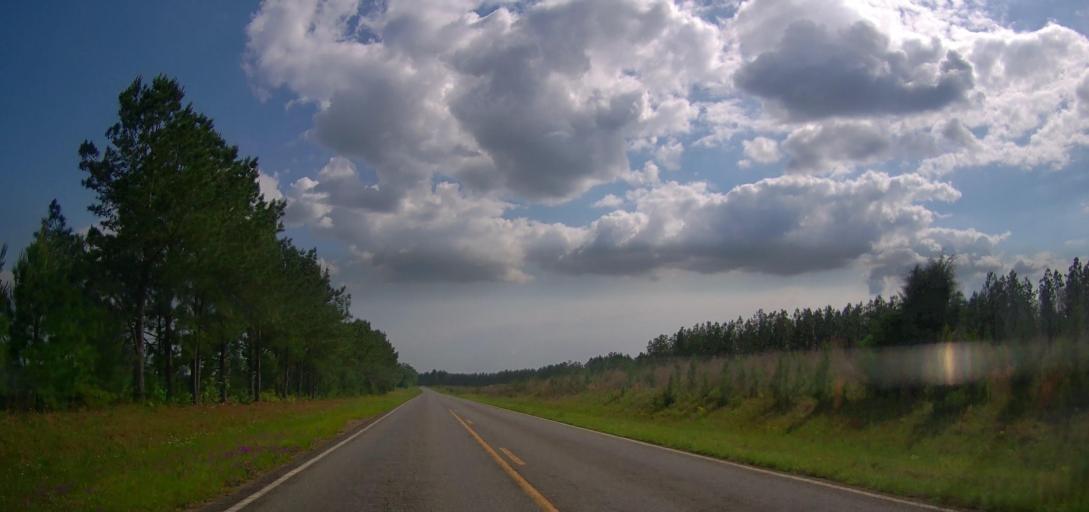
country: US
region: Georgia
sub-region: Laurens County
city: East Dublin
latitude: 32.7168
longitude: -82.9164
